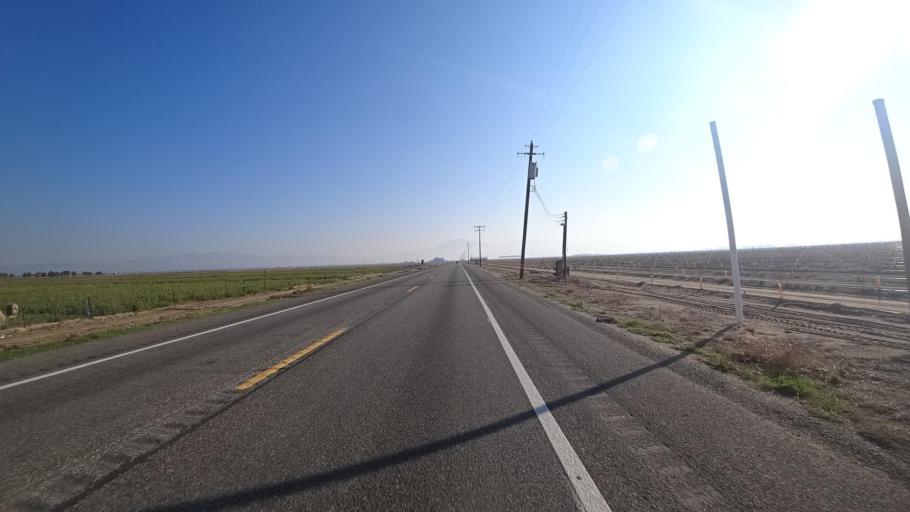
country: US
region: California
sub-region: Kern County
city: Greenfield
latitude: 35.2086
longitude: -118.9933
